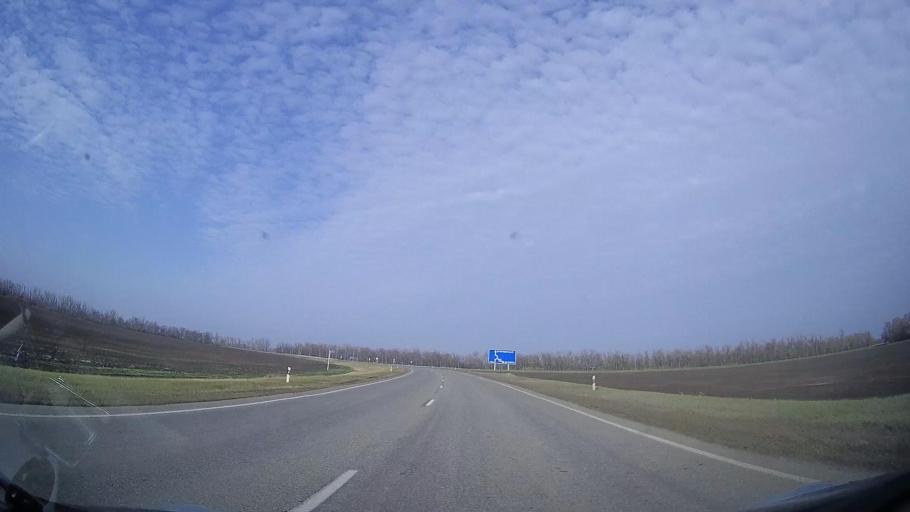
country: RU
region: Rostov
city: Tselina
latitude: 46.5289
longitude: 40.9898
